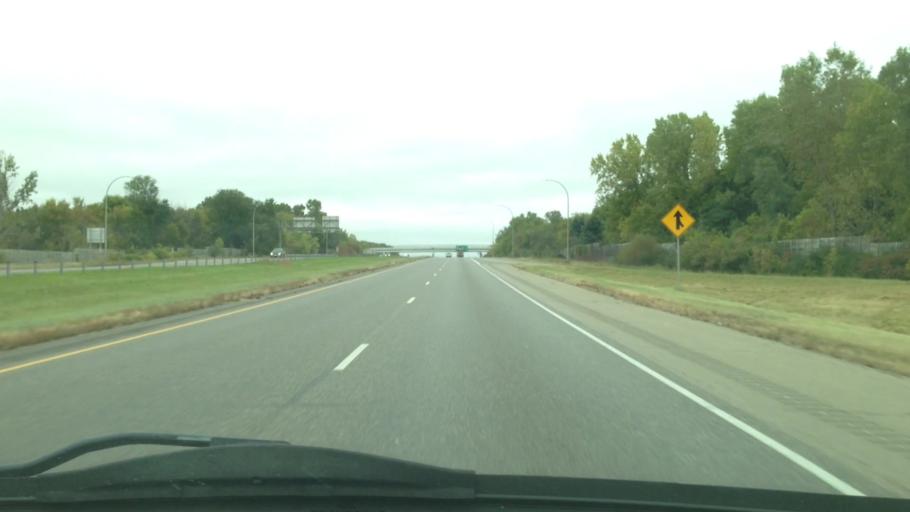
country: US
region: Minnesota
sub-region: Dakota County
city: Inver Grove Heights
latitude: 44.8362
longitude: -93.0595
